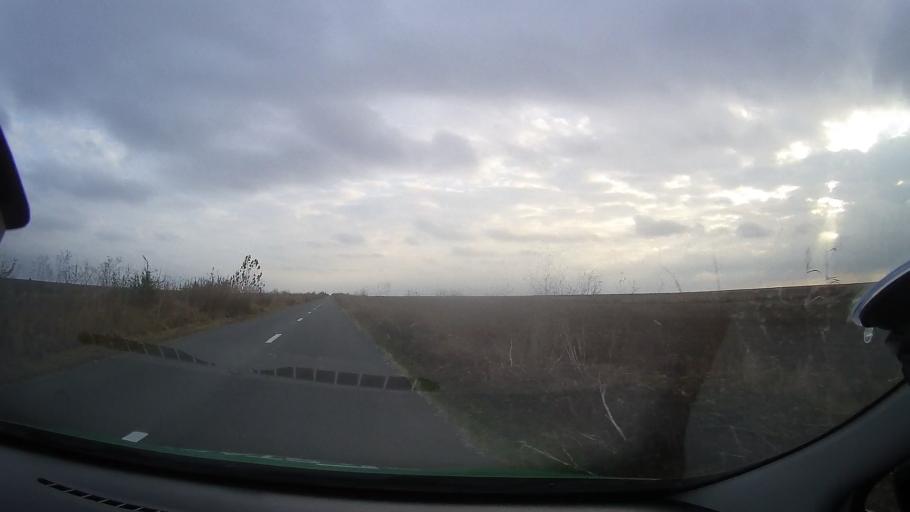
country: RO
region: Constanta
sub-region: Comuna Pestera
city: Pestera
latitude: 44.1458
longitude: 28.1154
